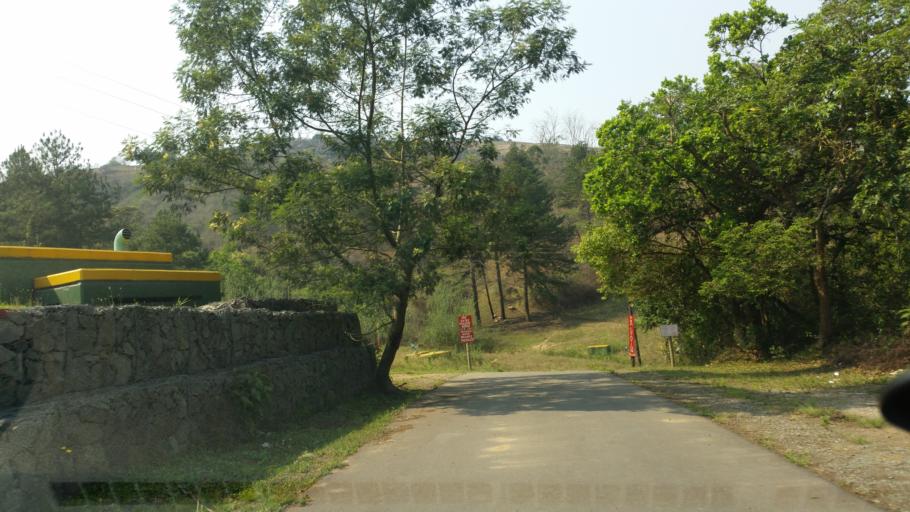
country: ZA
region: KwaZulu-Natal
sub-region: eThekwini Metropolitan Municipality
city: Mpumalanga
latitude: -29.7428
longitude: 30.6661
